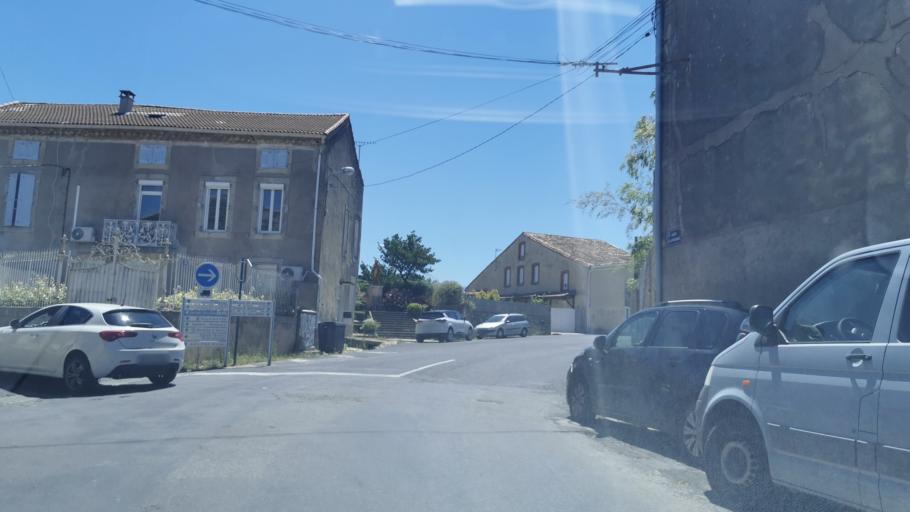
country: FR
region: Languedoc-Roussillon
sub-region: Departement de l'Herault
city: Nissan-lez-Enserune
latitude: 43.2873
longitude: 3.1275
